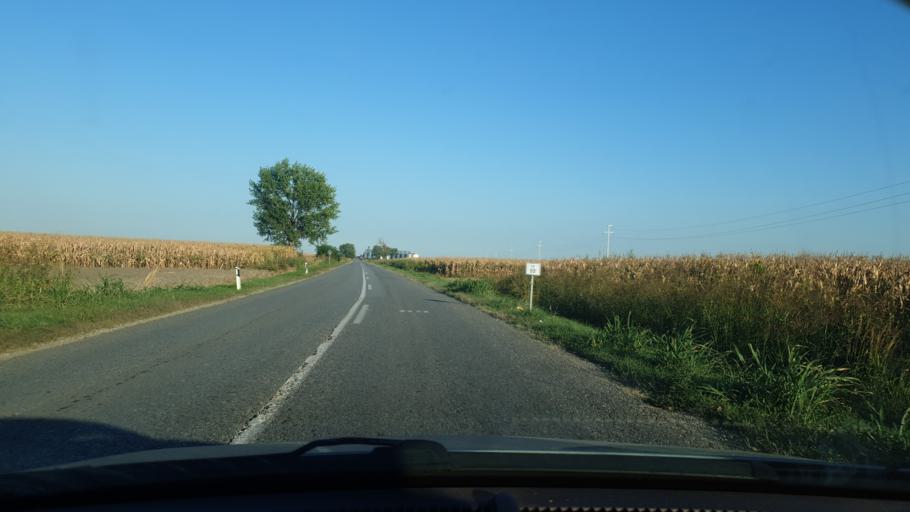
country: RS
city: Putinci
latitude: 44.9678
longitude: 19.9044
